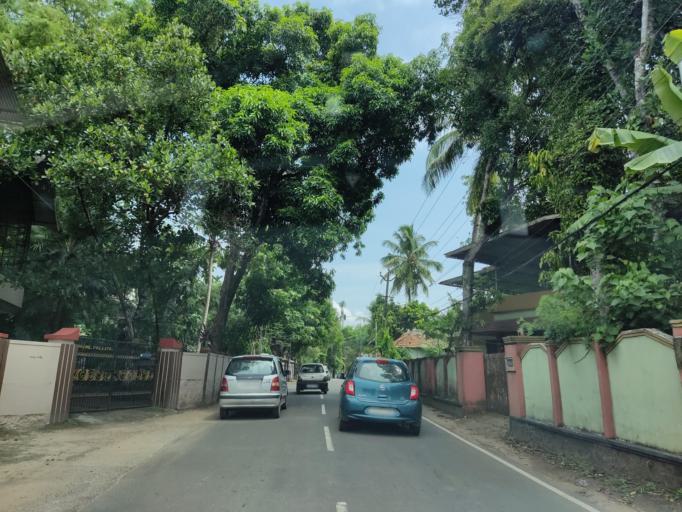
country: IN
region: Kerala
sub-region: Alappuzha
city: Chengannur
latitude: 9.3153
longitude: 76.6062
